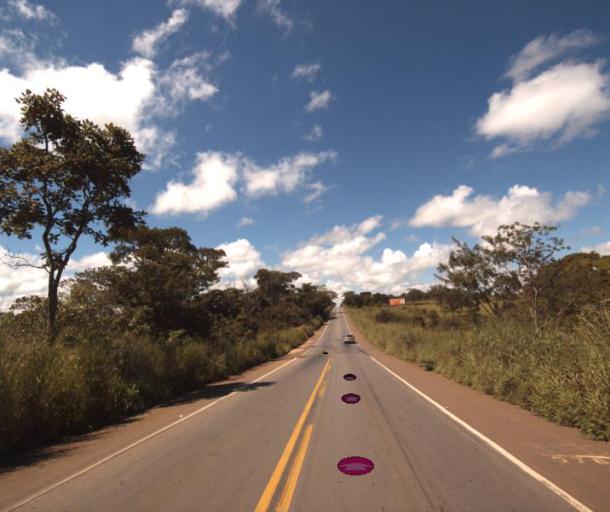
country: BR
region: Goias
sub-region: Jaragua
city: Jaragua
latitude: -15.8408
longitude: -49.2722
